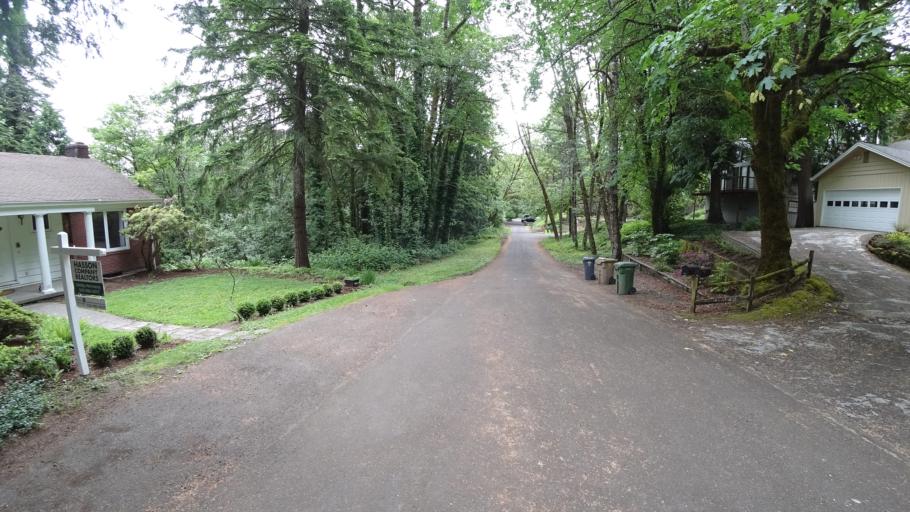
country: US
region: Oregon
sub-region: Clackamas County
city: Lake Oswego
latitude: 45.4285
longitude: -122.6733
